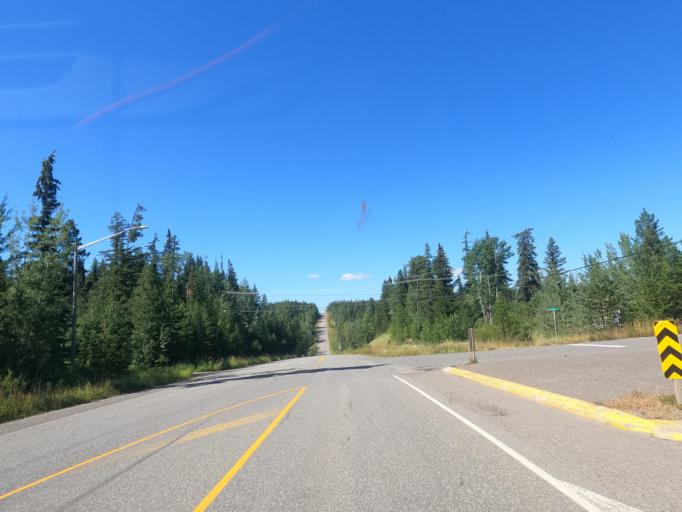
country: CA
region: British Columbia
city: Quesnel
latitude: 53.0319
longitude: -122.4087
